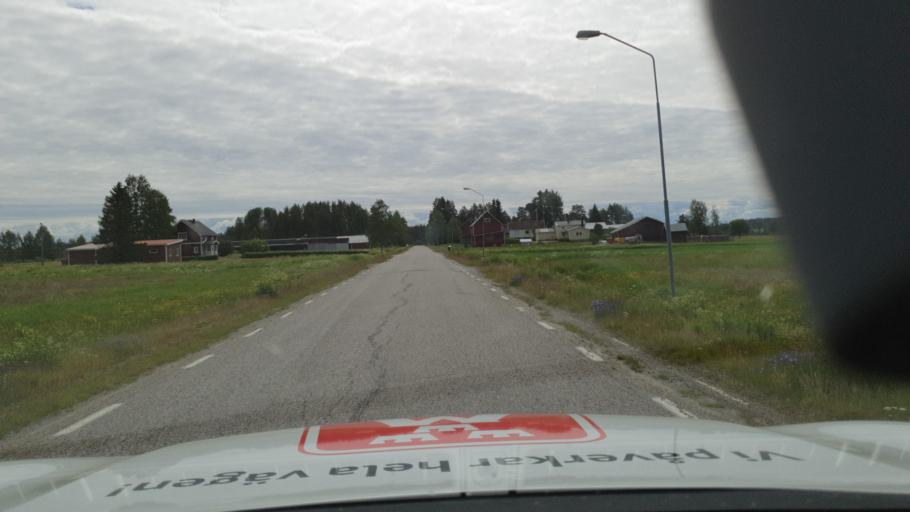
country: SE
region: Vaesterbotten
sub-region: Skelleftea Kommun
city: Forsbacka
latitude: 64.6205
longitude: 20.4969
